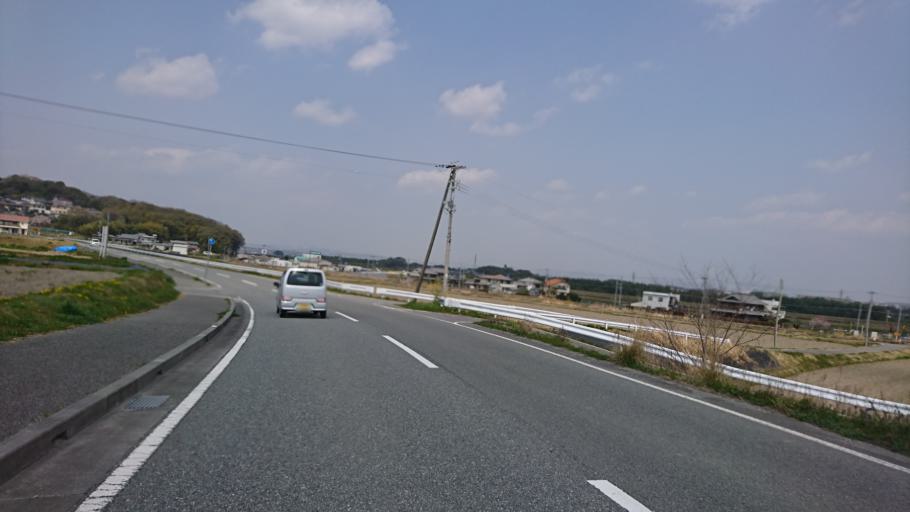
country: JP
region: Hyogo
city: Ono
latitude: 34.8384
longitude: 134.9108
